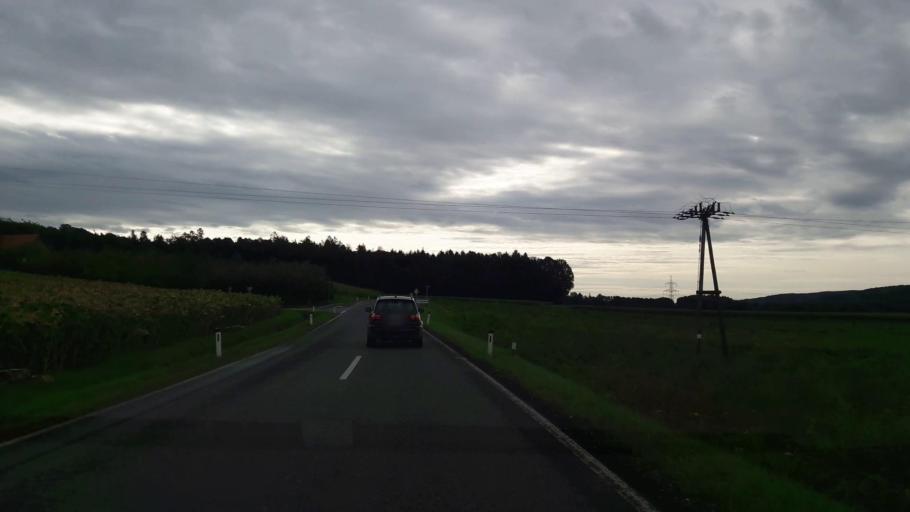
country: AT
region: Styria
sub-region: Politischer Bezirk Hartberg-Fuerstenfeld
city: Ebersdorf
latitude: 47.2109
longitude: 15.9349
